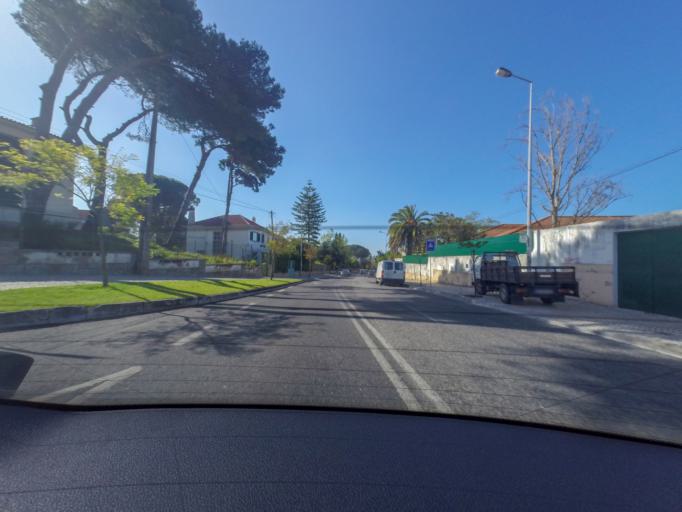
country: PT
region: Lisbon
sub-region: Cascais
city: Monte Estoril
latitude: 38.7053
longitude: -9.4178
